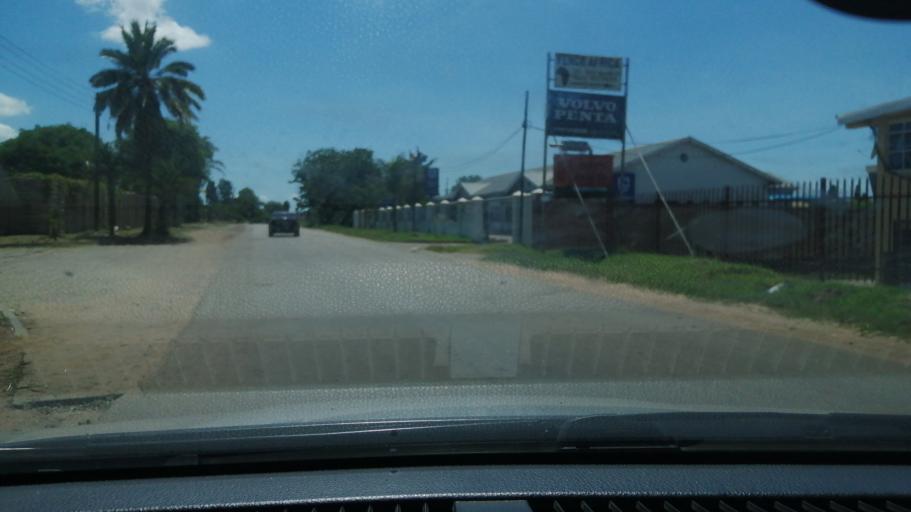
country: ZW
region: Harare
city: Epworth
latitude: -17.8444
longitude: 31.1163
